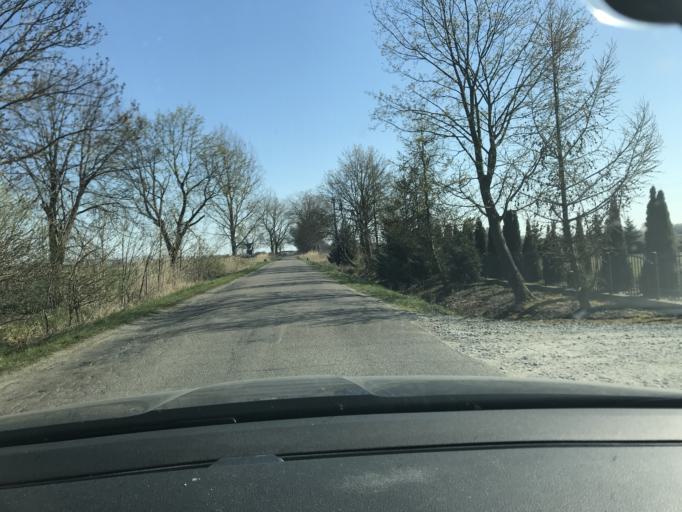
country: PL
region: Pomeranian Voivodeship
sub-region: Powiat nowodworski
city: Sztutowo
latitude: 54.3254
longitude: 19.1568
